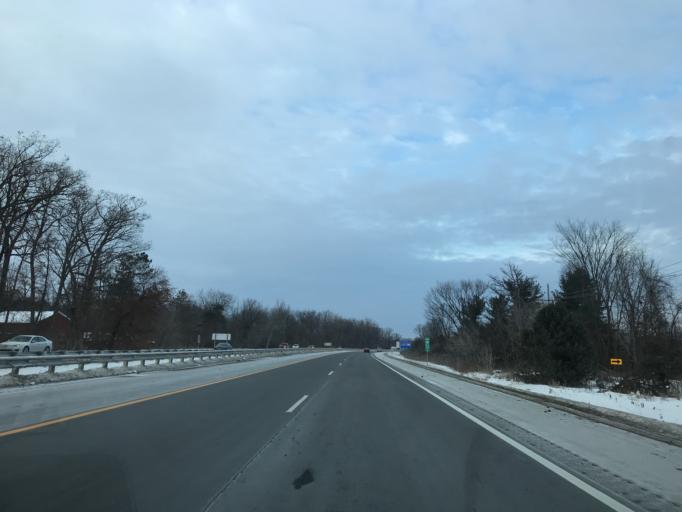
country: US
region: Michigan
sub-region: Livingston County
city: Whitmore Lake
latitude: 42.3857
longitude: -83.7605
